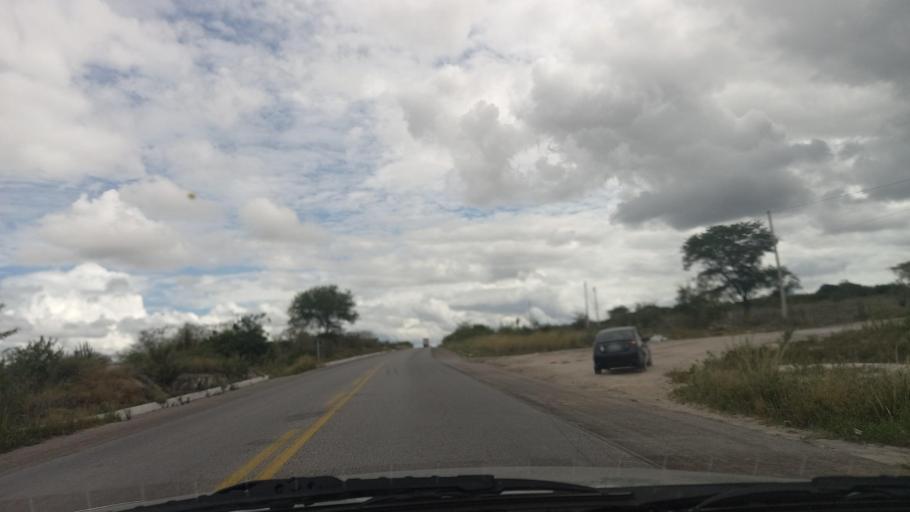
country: BR
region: Pernambuco
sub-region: Cachoeirinha
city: Cachoeirinha
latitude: -8.3440
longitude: -36.1634
